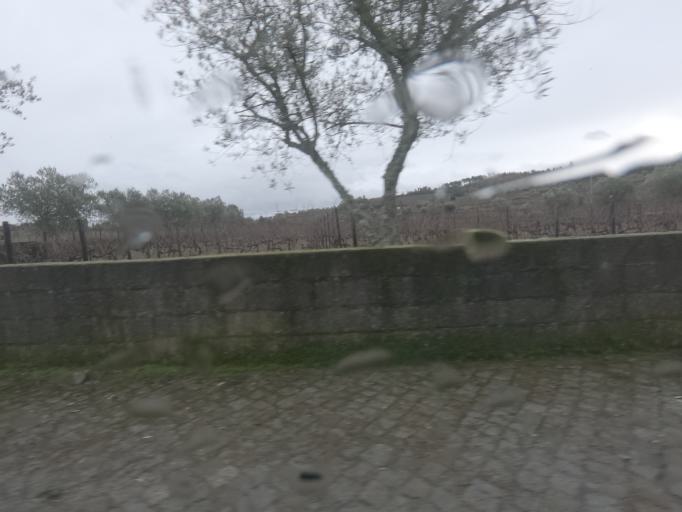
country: PT
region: Vila Real
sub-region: Peso da Regua
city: Peso da Regua
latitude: 41.1794
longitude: -7.7192
